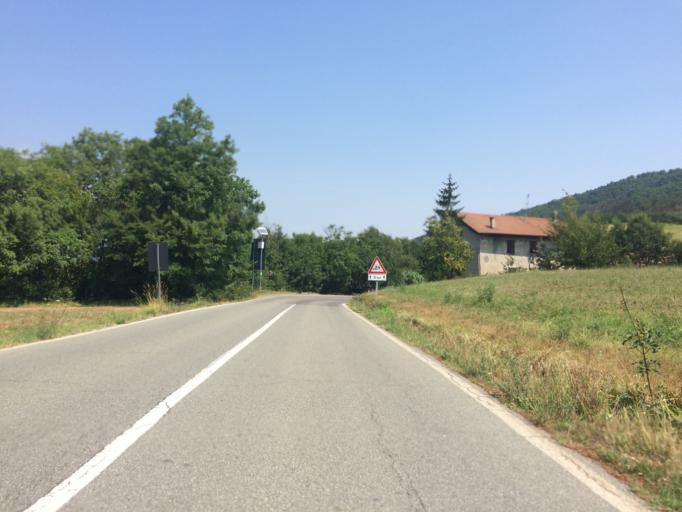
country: IT
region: Piedmont
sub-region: Provincia di Alessandria
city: Castelletto d'Erro
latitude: 44.6138
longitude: 8.4131
